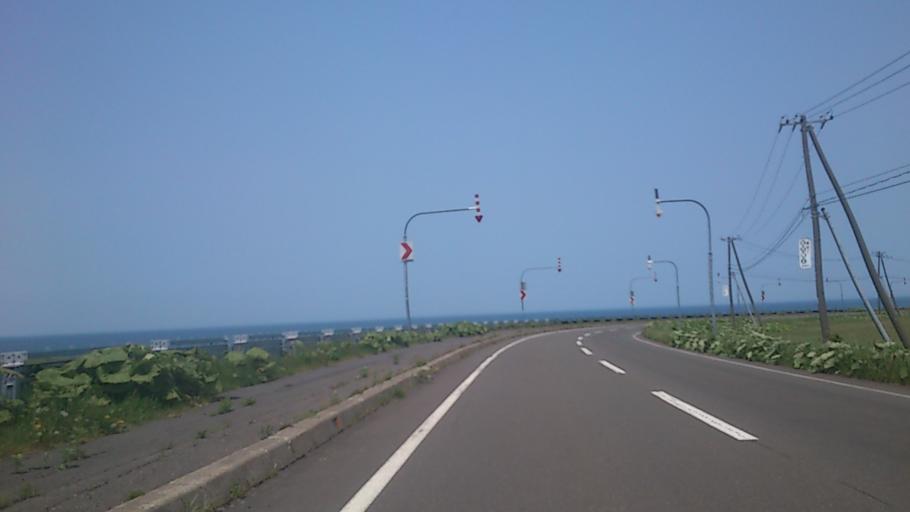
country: JP
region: Hokkaido
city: Nemuro
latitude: 43.3777
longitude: 145.6441
